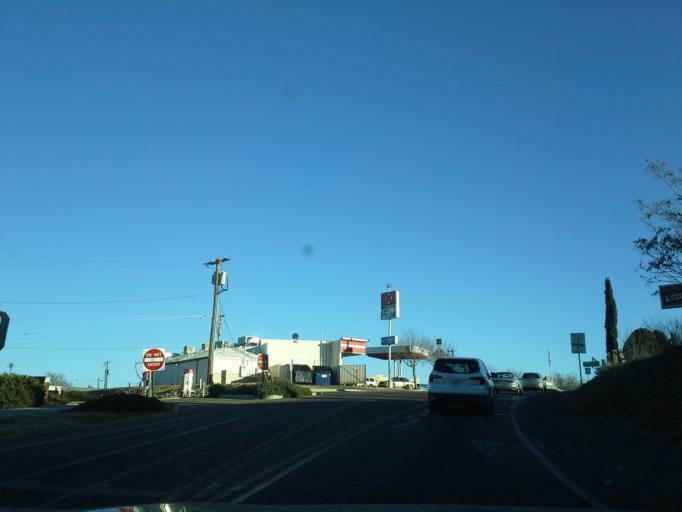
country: US
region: Arizona
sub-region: Yavapai County
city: Camp Verde
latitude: 34.5663
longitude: -111.8559
